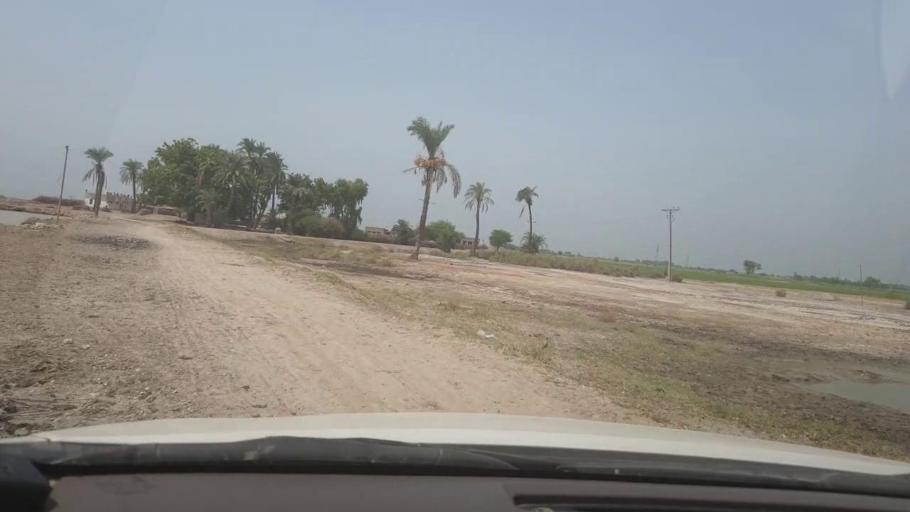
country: PK
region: Sindh
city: Shikarpur
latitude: 27.9620
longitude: 68.5907
